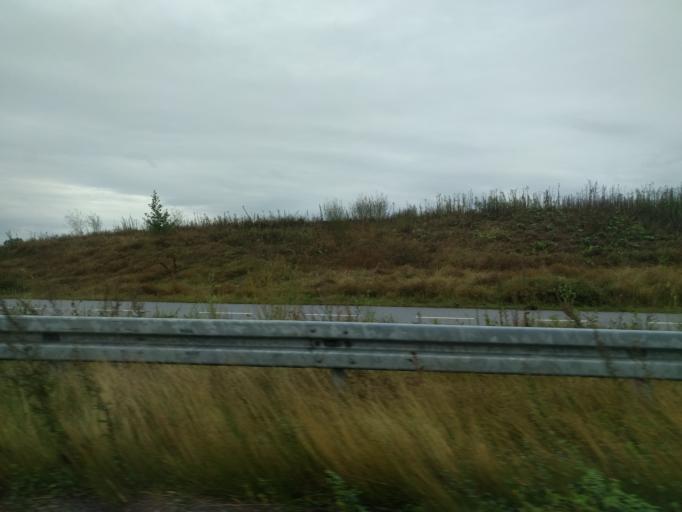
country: DK
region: Zealand
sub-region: Naestved Kommune
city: Fensmark
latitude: 55.2617
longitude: 11.7888
